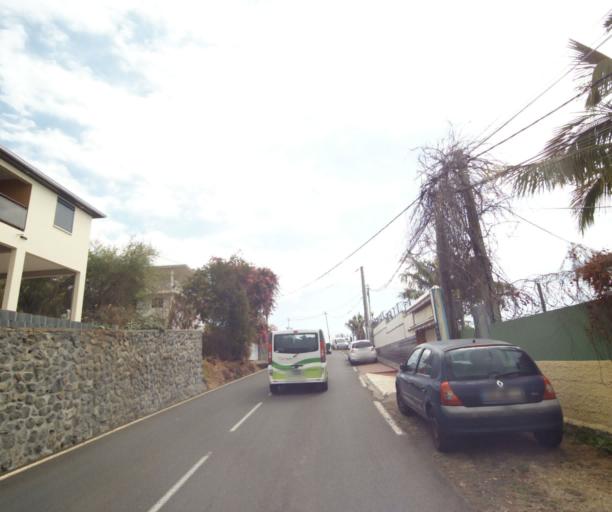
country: RE
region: Reunion
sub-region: Reunion
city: Saint-Paul
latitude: -21.0171
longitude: 55.2876
